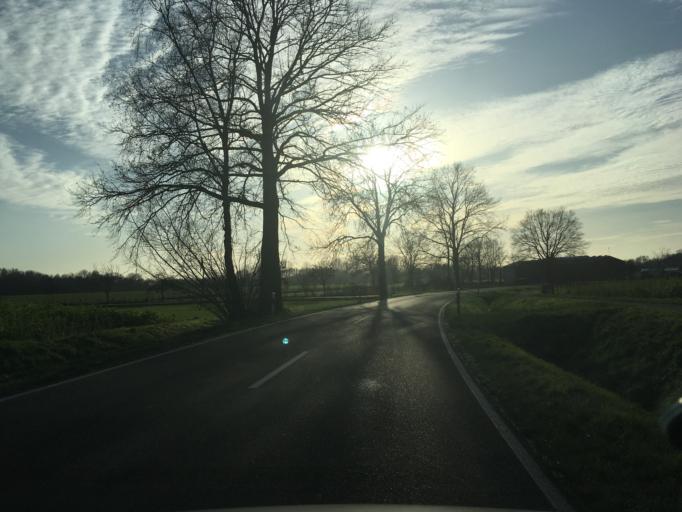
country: DE
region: North Rhine-Westphalia
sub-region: Regierungsbezirk Munster
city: Gescher
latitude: 51.9471
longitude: 7.0551
